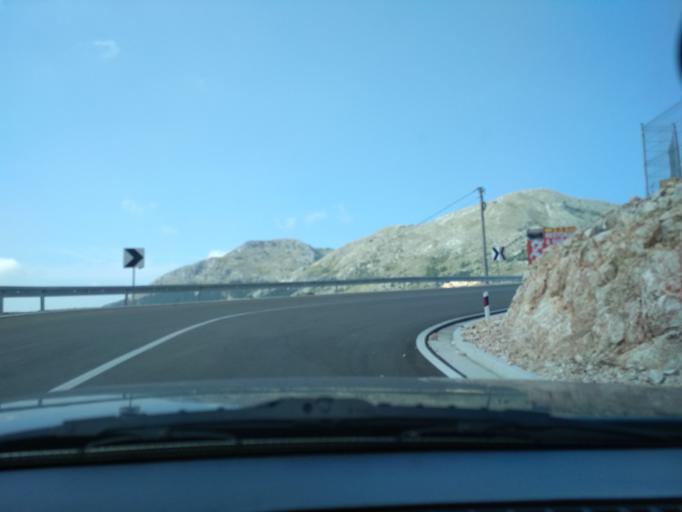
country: ME
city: Dobrota
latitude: 42.4387
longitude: 18.8363
